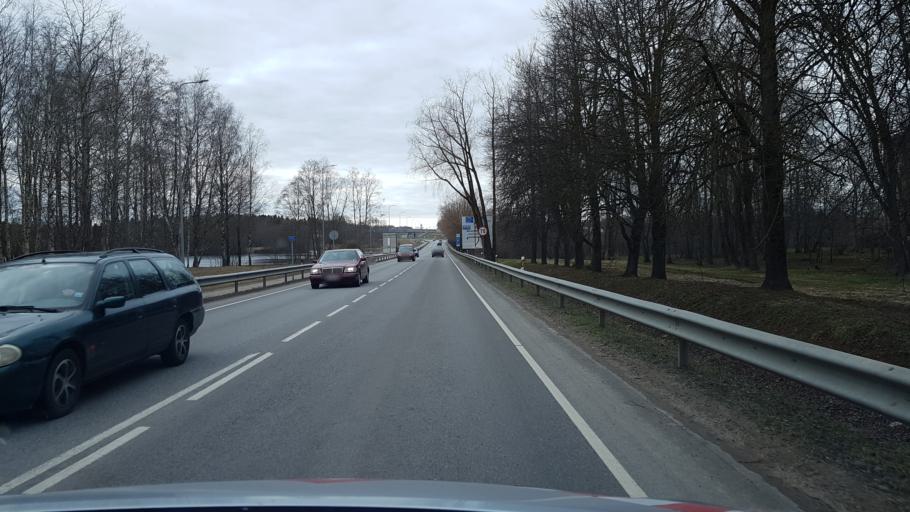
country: EE
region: Ida-Virumaa
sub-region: Sillamaee linn
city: Sillamae
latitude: 59.3910
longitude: 27.7626
